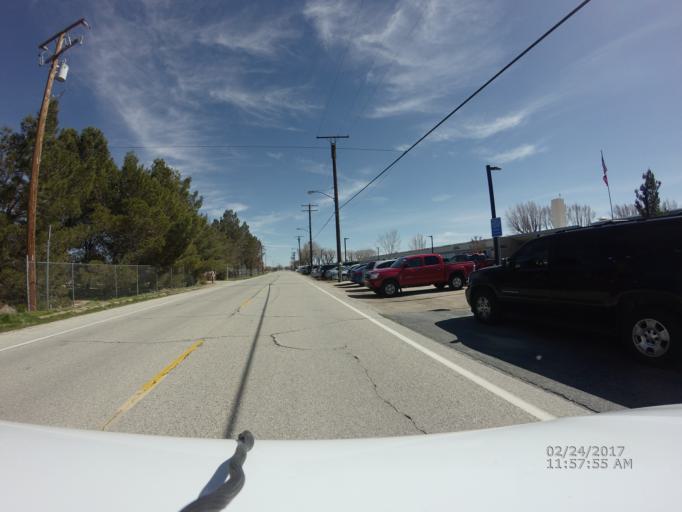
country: US
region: California
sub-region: Los Angeles County
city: Lancaster
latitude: 34.7193
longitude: -118.0088
